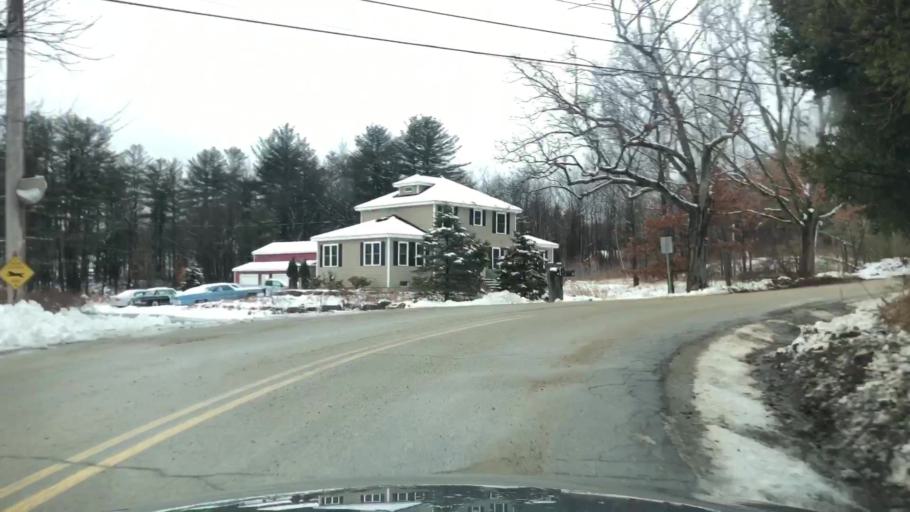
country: US
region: New Hampshire
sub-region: Hillsborough County
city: Mont Vernon
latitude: 42.9362
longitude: -71.6132
